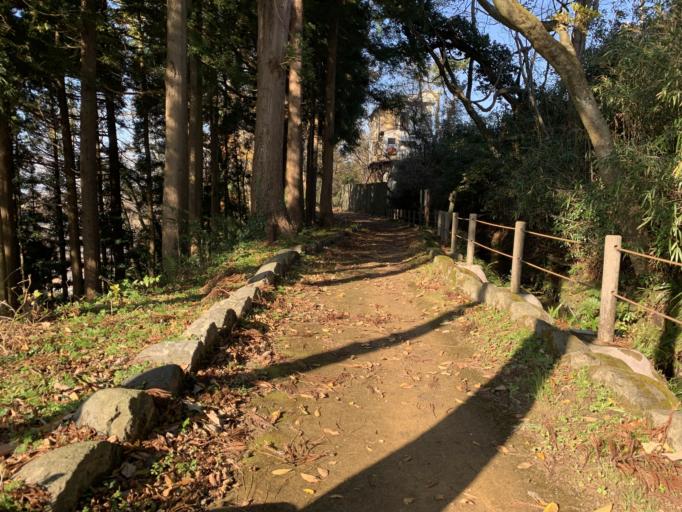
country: JP
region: Ishikawa
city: Nonoichi
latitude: 36.5380
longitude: 136.6870
